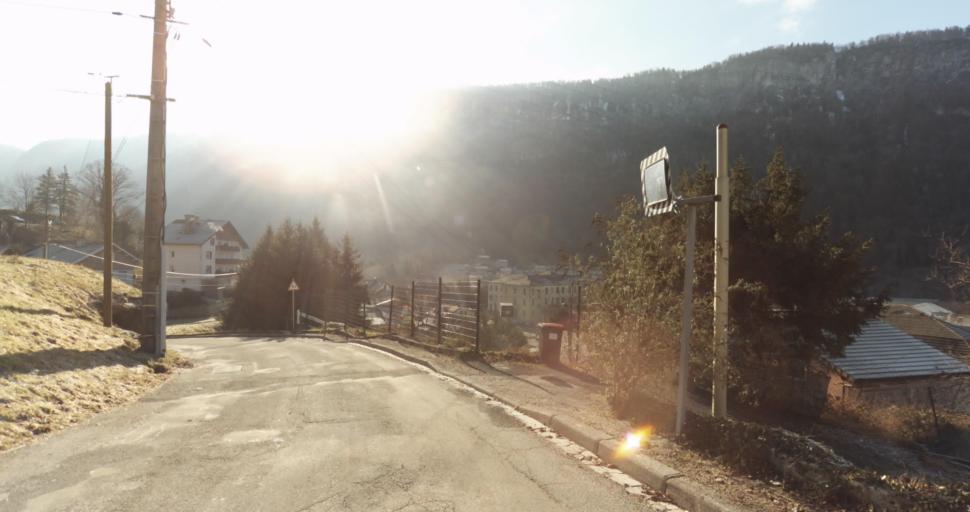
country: FR
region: Rhone-Alpes
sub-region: Departement de l'Ain
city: Nantua
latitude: 46.1503
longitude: 5.6090
